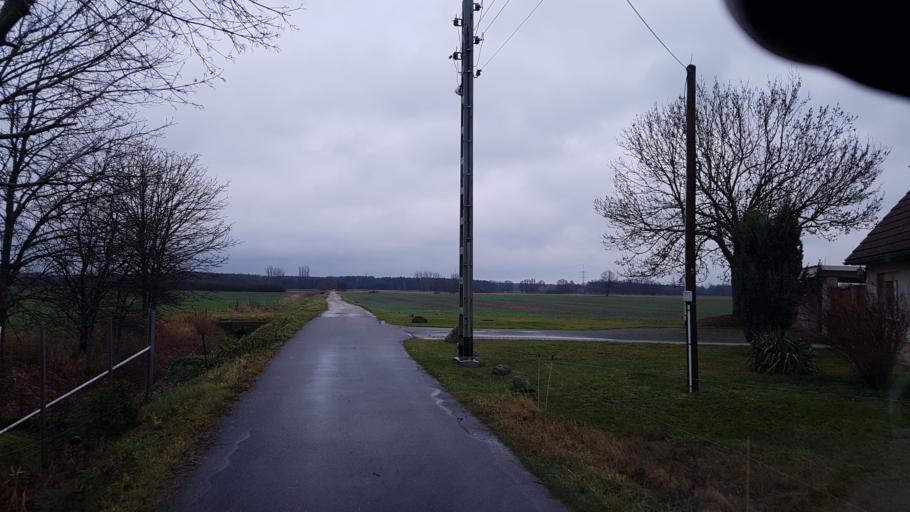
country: DE
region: Brandenburg
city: Sallgast
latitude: 51.6383
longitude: 13.8629
